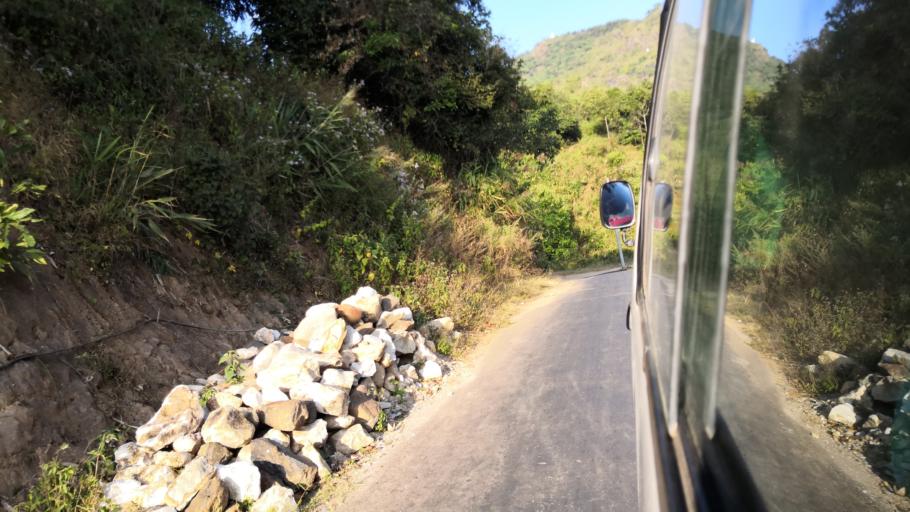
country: MM
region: Mandalay
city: Mogok
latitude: 22.9043
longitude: 96.3885
